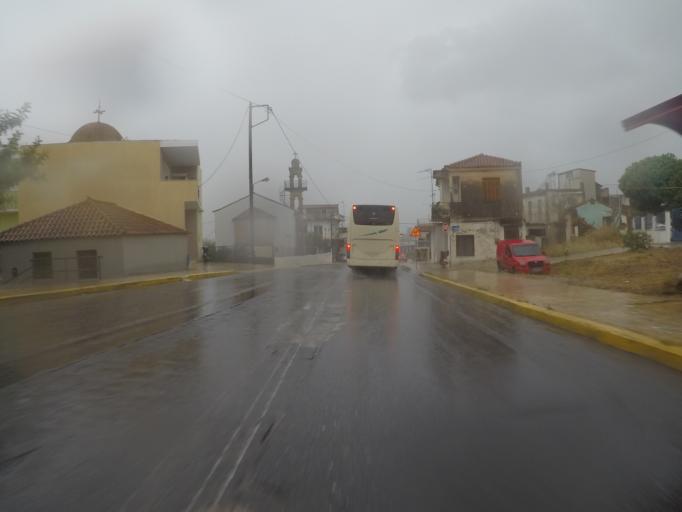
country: GR
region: Peloponnese
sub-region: Nomos Messinias
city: Sperkhoyia
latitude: 37.0479
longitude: 22.0746
